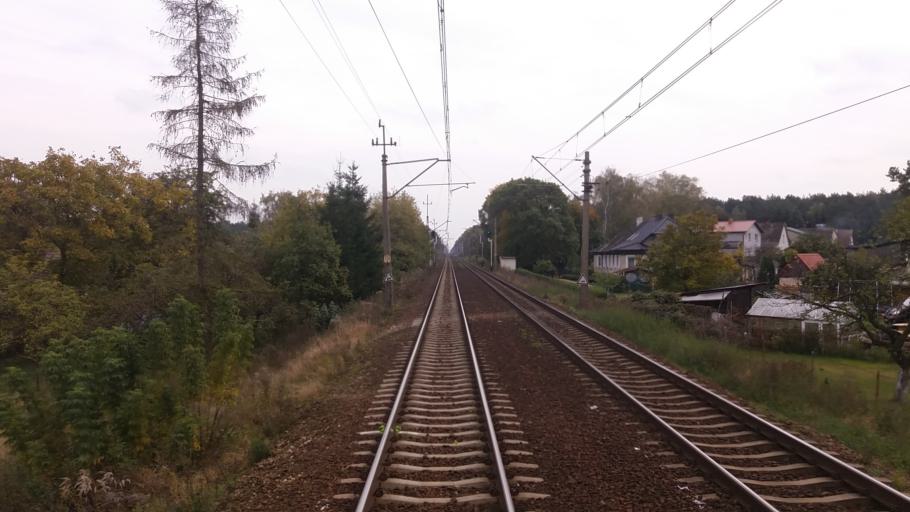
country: PL
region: West Pomeranian Voivodeship
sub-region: Powiat gryfinski
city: Stare Czarnowo
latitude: 53.3842
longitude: 14.7547
